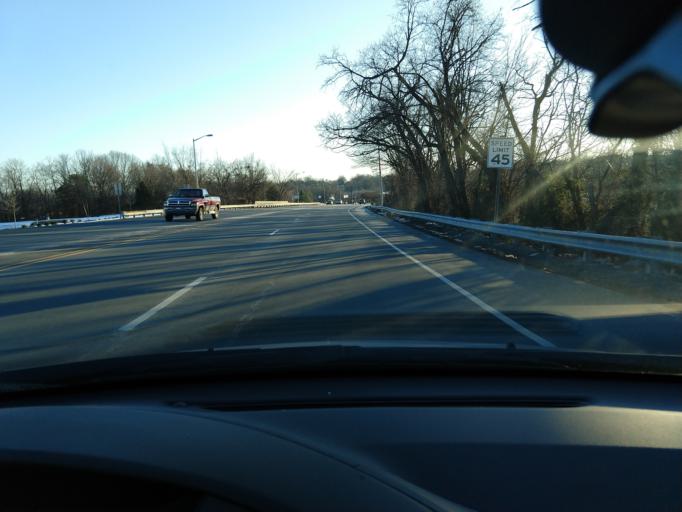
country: US
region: North Carolina
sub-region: Guilford County
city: Greensboro
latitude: 36.0607
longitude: -79.8006
